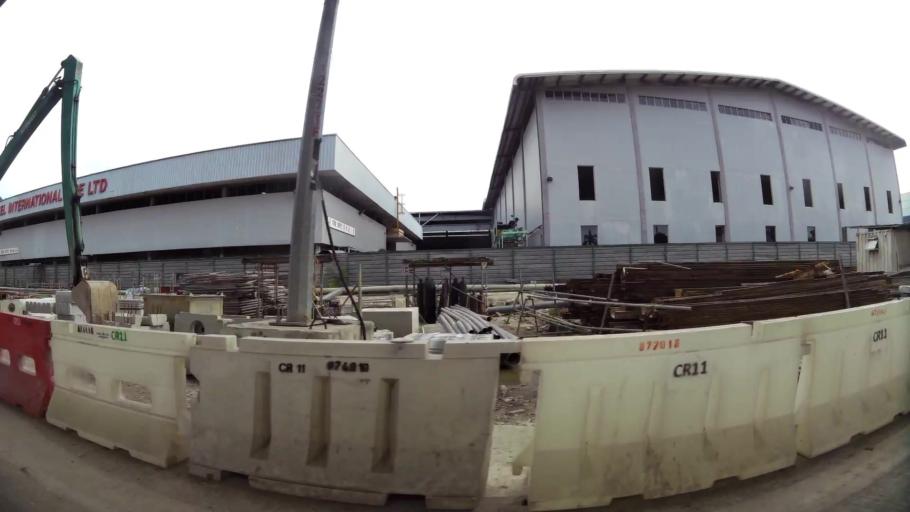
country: MY
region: Johor
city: Johor Bahru
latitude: 1.3199
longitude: 103.6504
